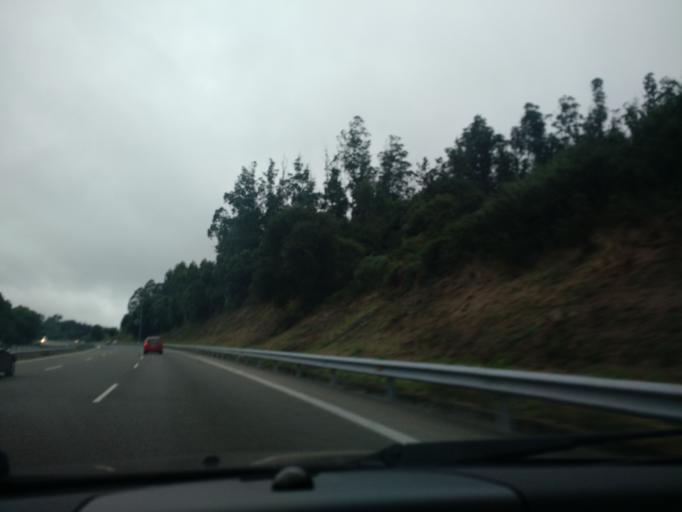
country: ES
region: Galicia
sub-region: Provincia da Coruna
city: Abegondo
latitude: 43.1865
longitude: -8.3114
